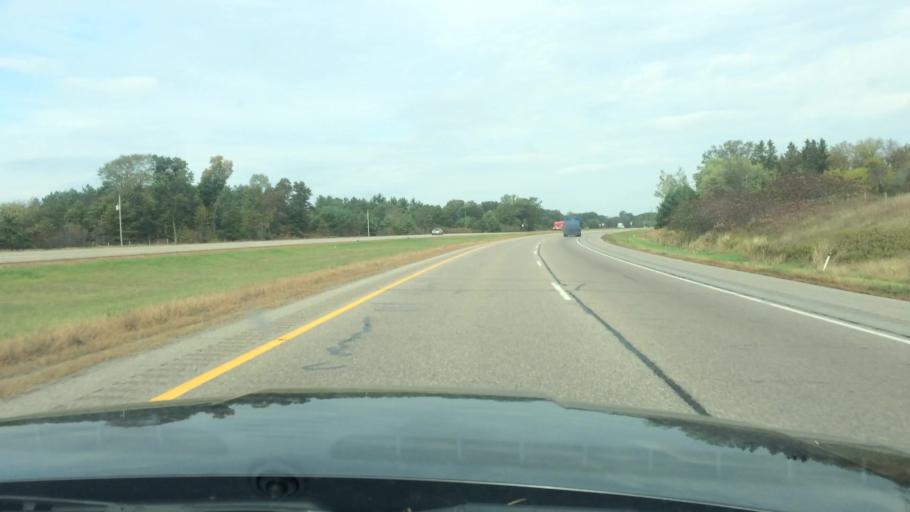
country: US
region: Wisconsin
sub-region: Marathon County
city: Mosinee
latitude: 44.6605
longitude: -89.6426
